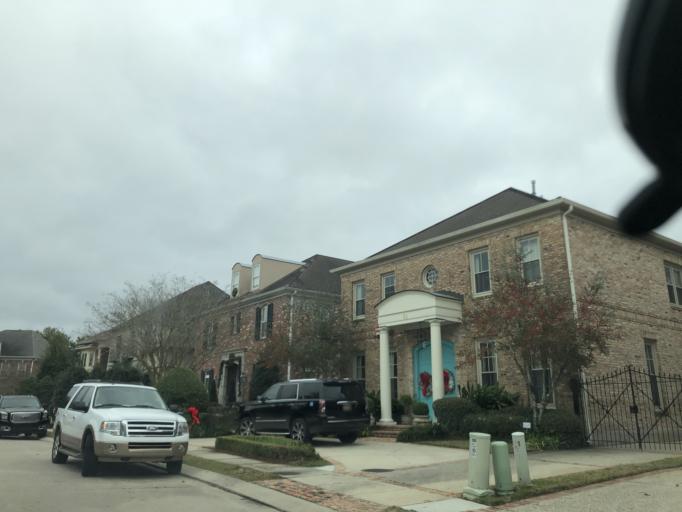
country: US
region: Louisiana
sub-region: Jefferson Parish
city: Metairie
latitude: 29.9769
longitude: -90.1517
